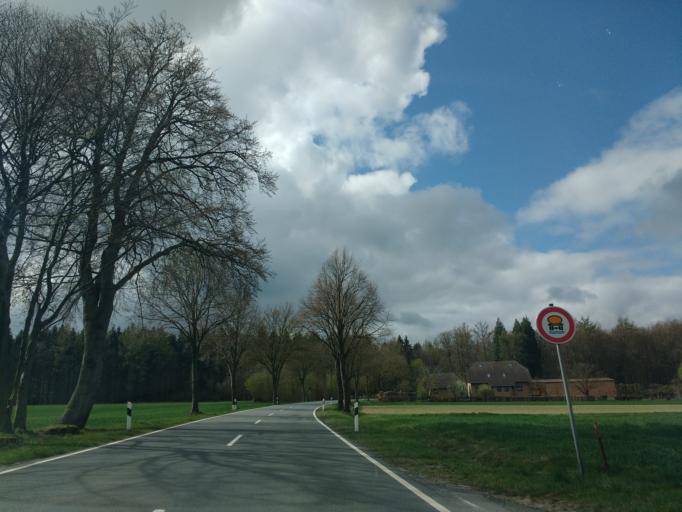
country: DE
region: North Rhine-Westphalia
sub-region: Regierungsbezirk Detmold
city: Wunnenberg
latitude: 51.5021
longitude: 8.7388
